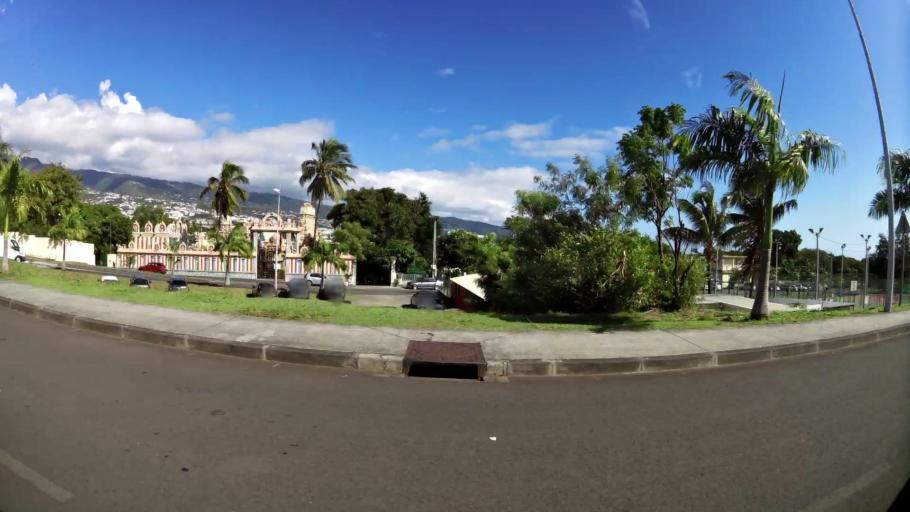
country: RE
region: Reunion
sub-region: Reunion
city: Sainte-Marie
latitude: -20.8977
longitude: 55.5019
